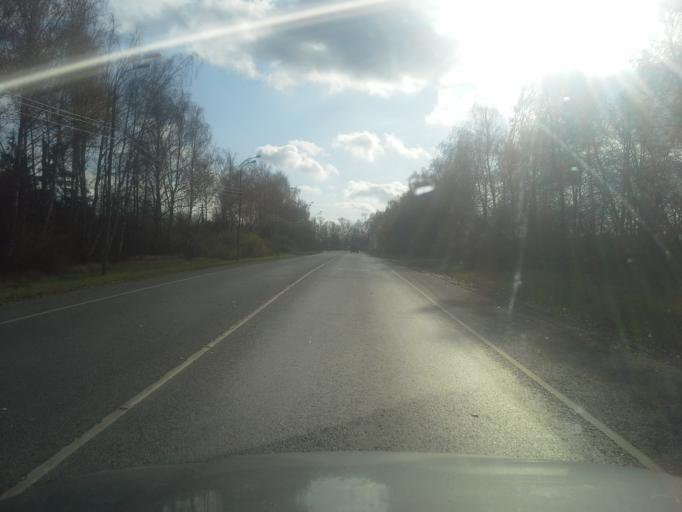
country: RU
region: Moskovskaya
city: Zvenigorod
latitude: 55.6855
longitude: 36.9007
